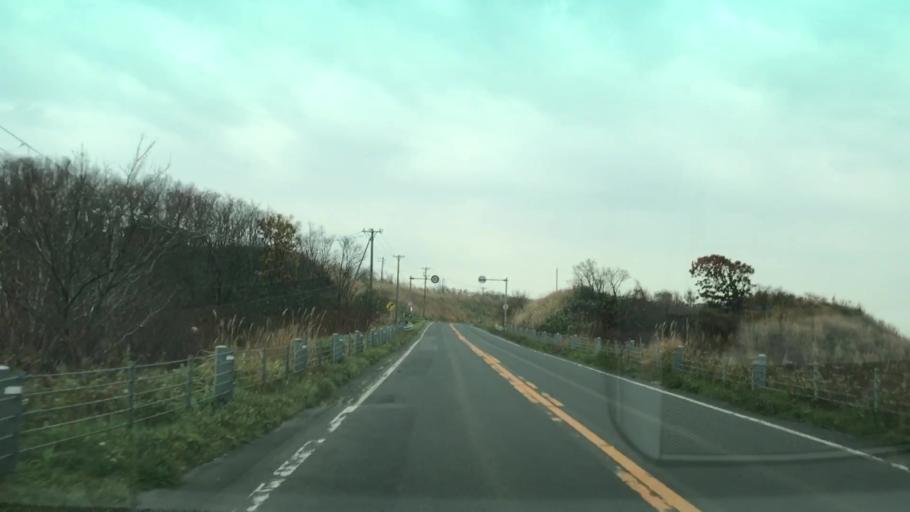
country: JP
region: Hokkaido
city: Ishikari
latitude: 43.3870
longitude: 141.4326
